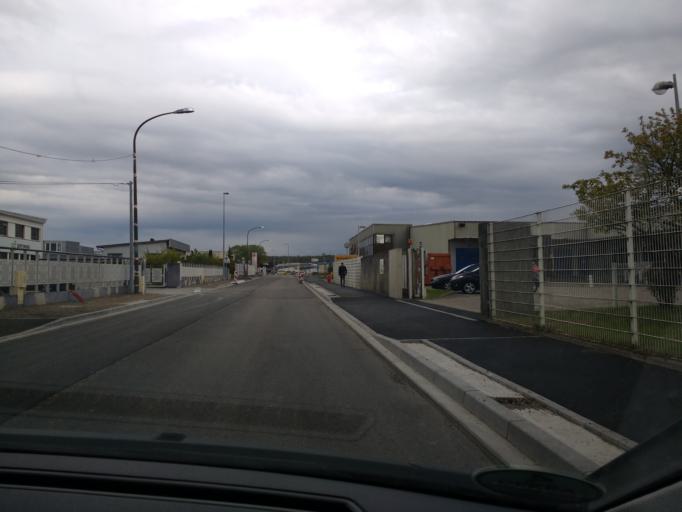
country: FR
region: Lorraine
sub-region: Departement de la Moselle
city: Remelfing
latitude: 49.1101
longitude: 7.0926
